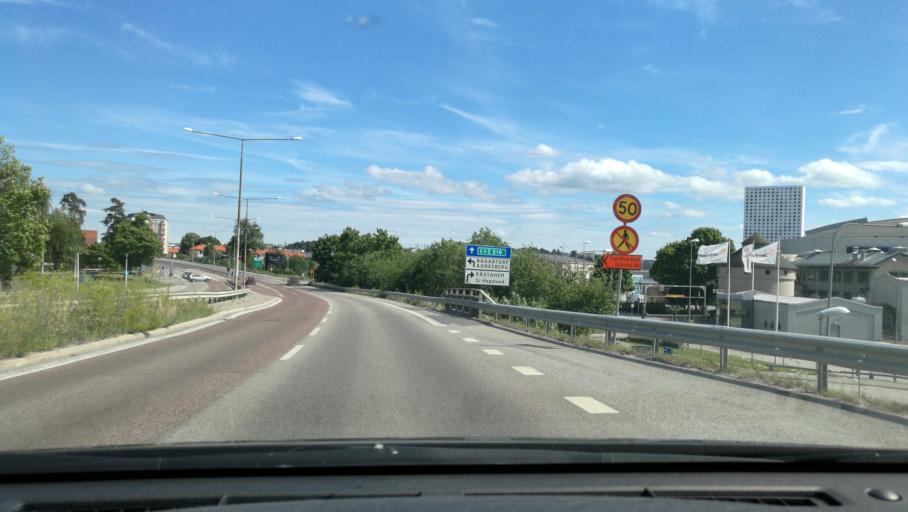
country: SE
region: Stockholm
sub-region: Solna Kommun
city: Rasunda
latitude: 59.3776
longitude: 17.9969
